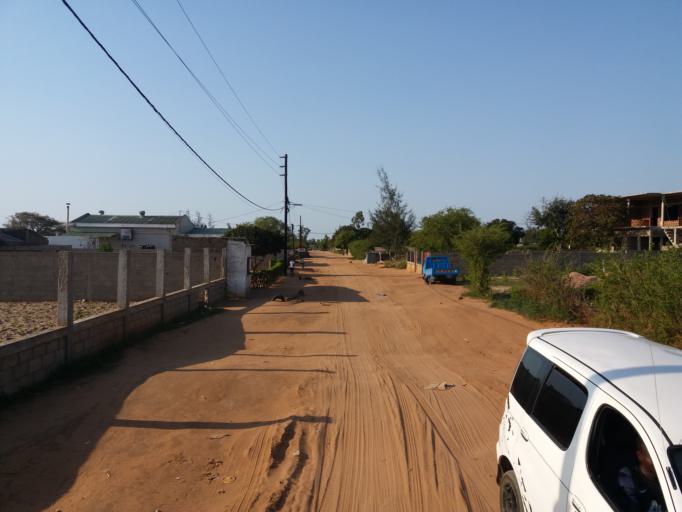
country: MZ
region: Maputo City
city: Maputo
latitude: -25.7662
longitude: 32.6084
